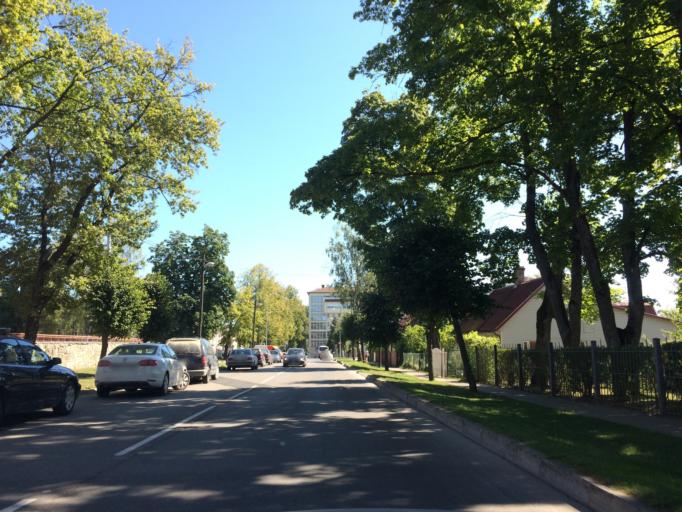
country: LV
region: Rezekne
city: Rezekne
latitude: 56.5090
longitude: 27.3395
